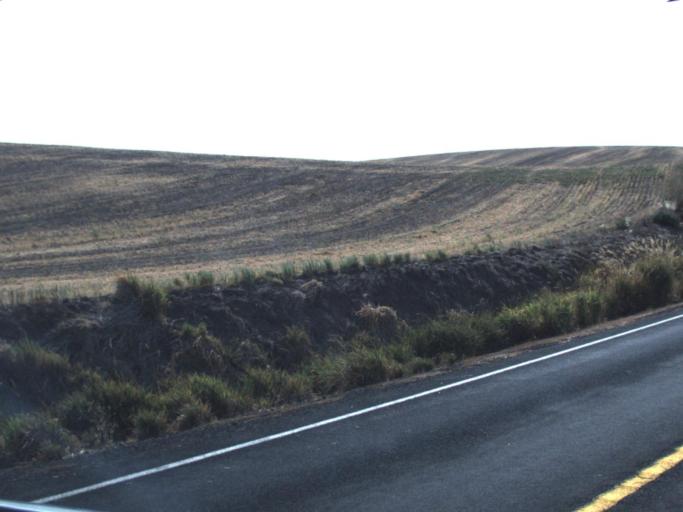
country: US
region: Washington
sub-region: Whitman County
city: Colfax
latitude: 47.0352
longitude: -117.1541
